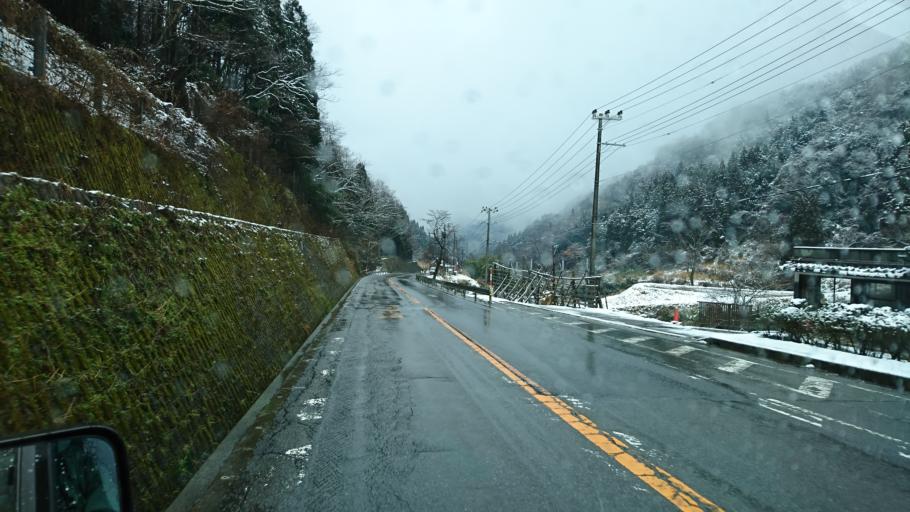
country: JP
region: Tottori
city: Tottori
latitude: 35.5258
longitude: 134.5189
